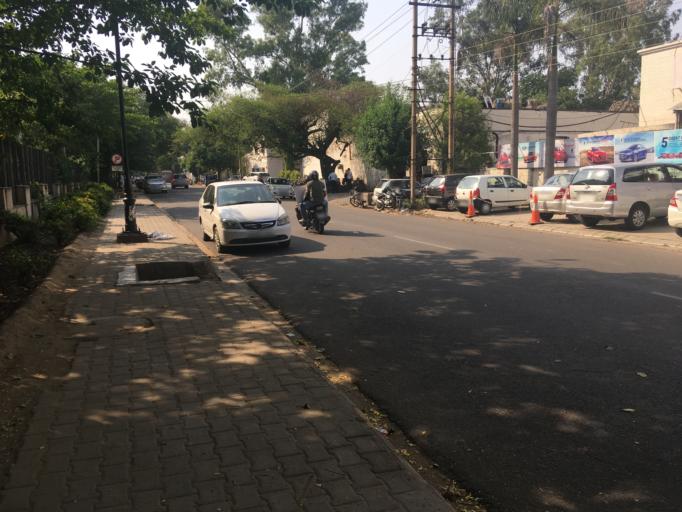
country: IN
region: Chandigarh
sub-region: Chandigarh
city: Chandigarh
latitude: 30.7053
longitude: 76.8025
